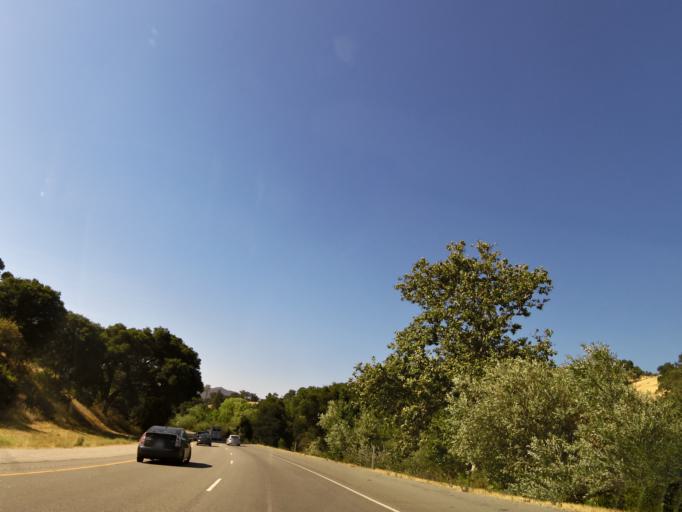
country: US
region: California
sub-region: San Luis Obispo County
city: Santa Margarita
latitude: 35.3637
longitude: -120.6381
